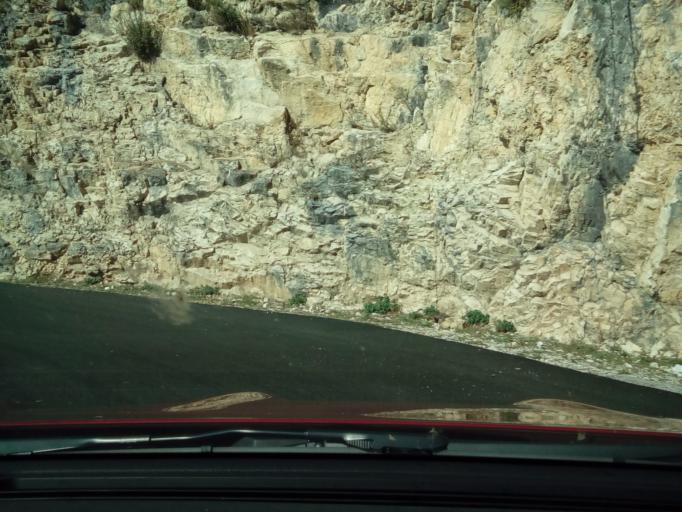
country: FR
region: Rhone-Alpes
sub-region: Departement de la Drome
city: Die
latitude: 44.8700
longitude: 5.4102
